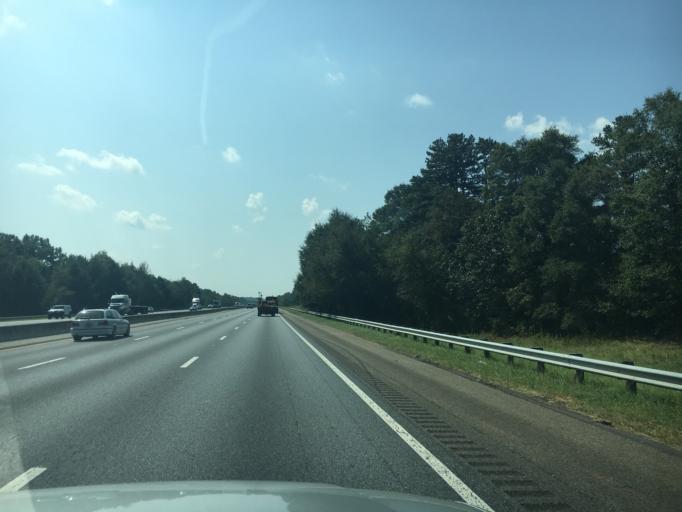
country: US
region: South Carolina
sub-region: Greenville County
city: Golden Grove
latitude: 34.7506
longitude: -82.4794
